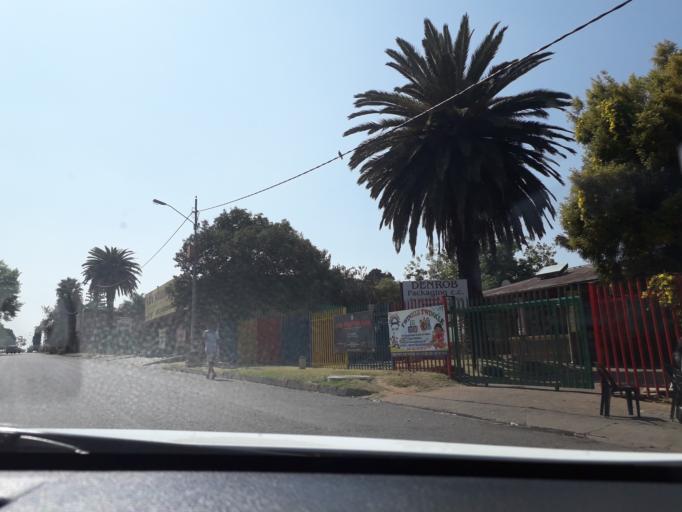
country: ZA
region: Gauteng
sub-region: City of Johannesburg Metropolitan Municipality
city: Modderfontein
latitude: -26.1105
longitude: 28.2322
